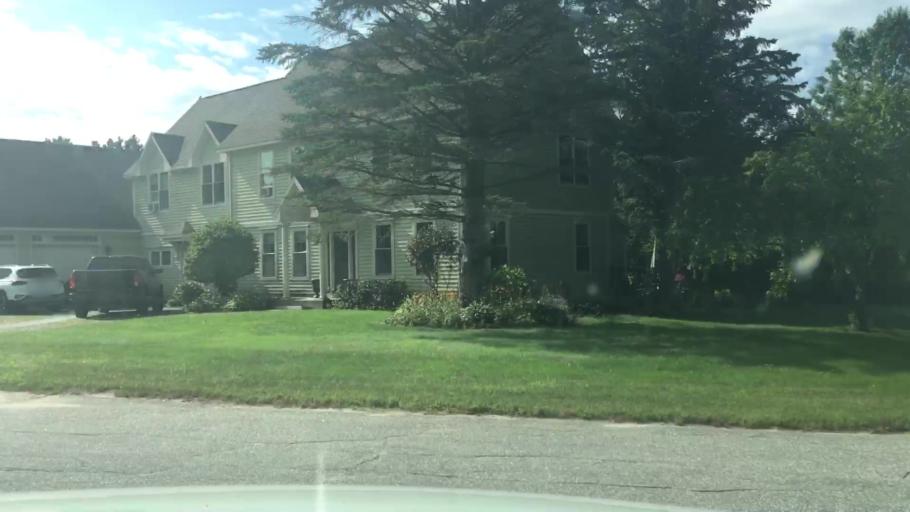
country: US
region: Maine
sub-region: Androscoggin County
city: Lewiston
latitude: 44.1152
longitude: -70.2023
